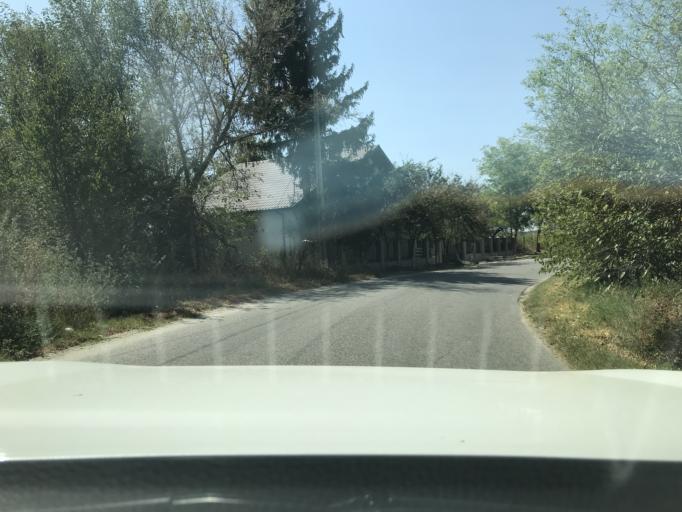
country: RO
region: Olt
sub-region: Comuna Falcoiu
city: Falcoiu
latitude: 44.2354
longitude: 24.3654
